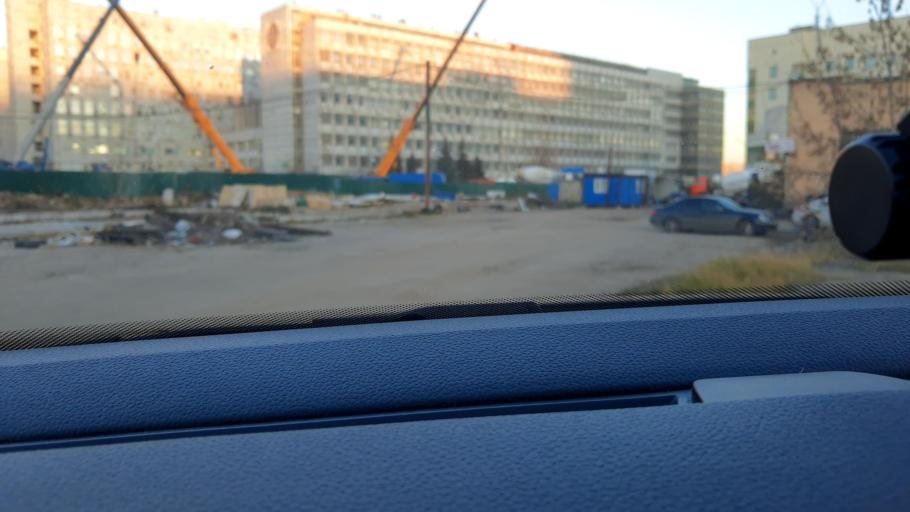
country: RU
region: Moskovskaya
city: Cheremushki
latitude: 55.6587
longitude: 37.5370
